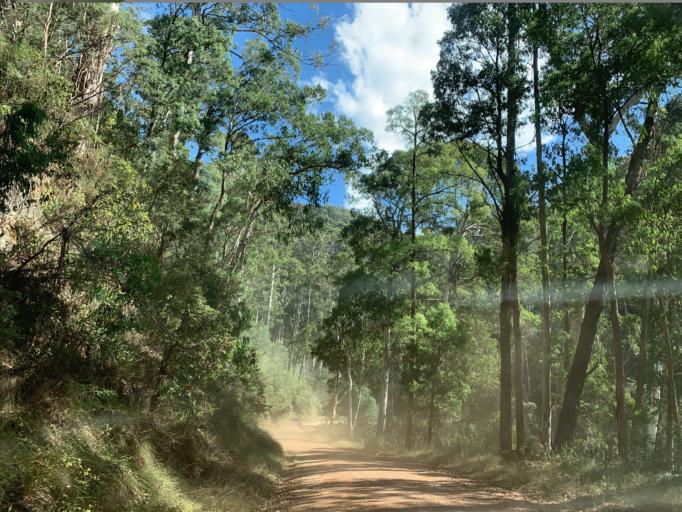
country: AU
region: Victoria
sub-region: Mansfield
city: Mansfield
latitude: -37.0936
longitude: 146.5200
